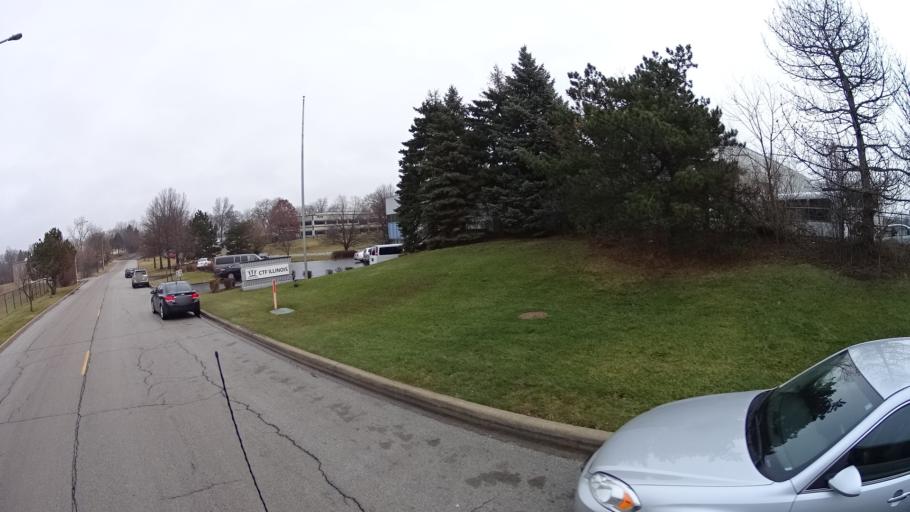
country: US
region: Illinois
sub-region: Cook County
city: Hazel Crest
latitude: 41.5738
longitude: -87.6776
